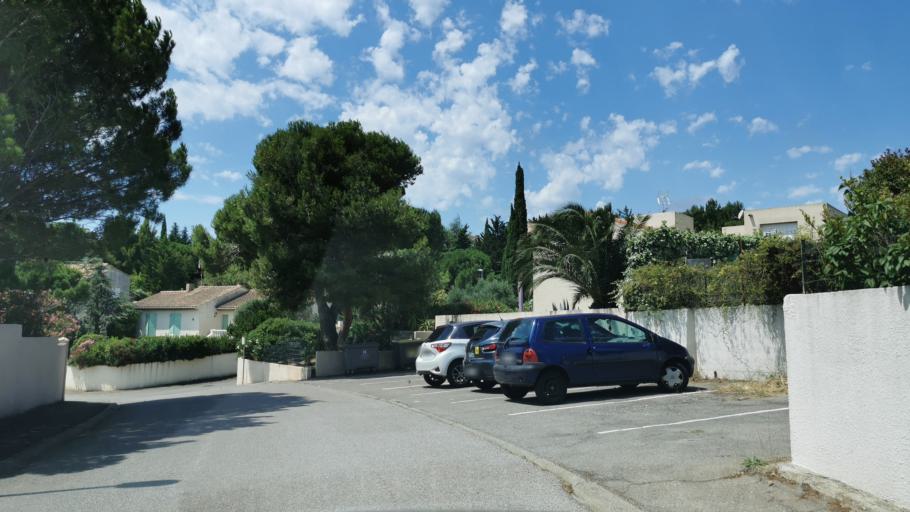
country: FR
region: Languedoc-Roussillon
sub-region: Departement de l'Aude
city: Narbonne
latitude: 43.1433
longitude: 2.9647
